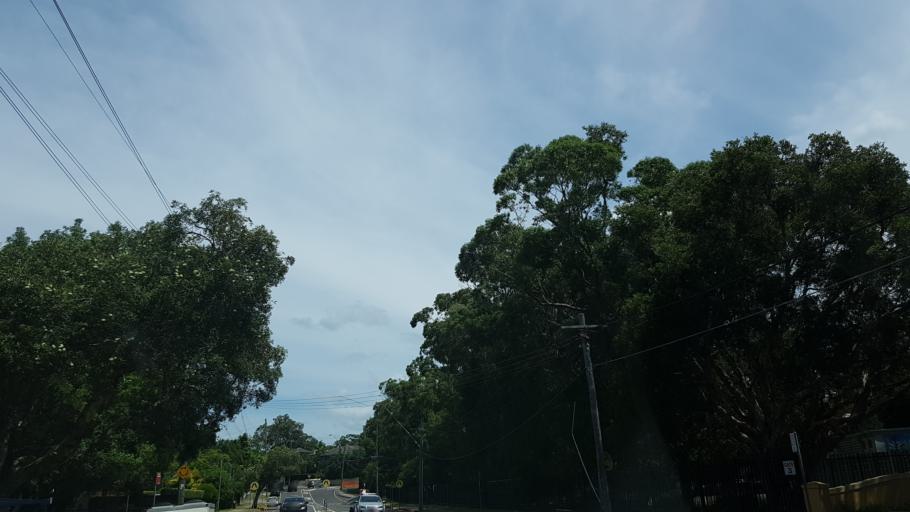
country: AU
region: New South Wales
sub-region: Pittwater
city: Bay View
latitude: -33.6693
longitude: 151.3037
